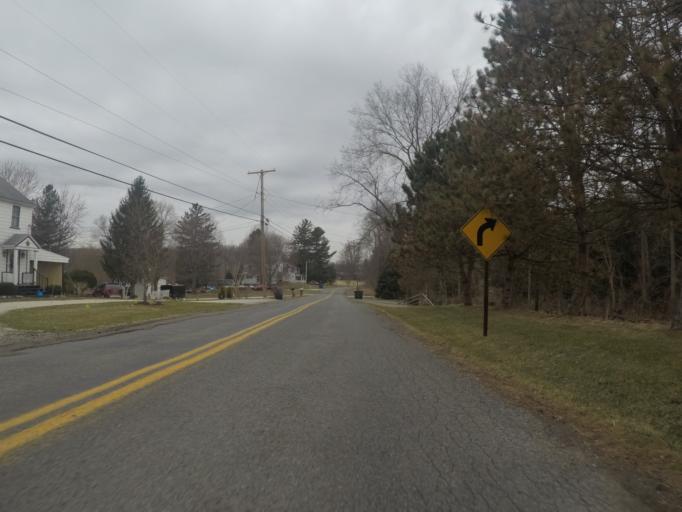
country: US
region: Ohio
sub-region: Portage County
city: Ravenna
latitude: 41.1737
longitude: -81.2904
